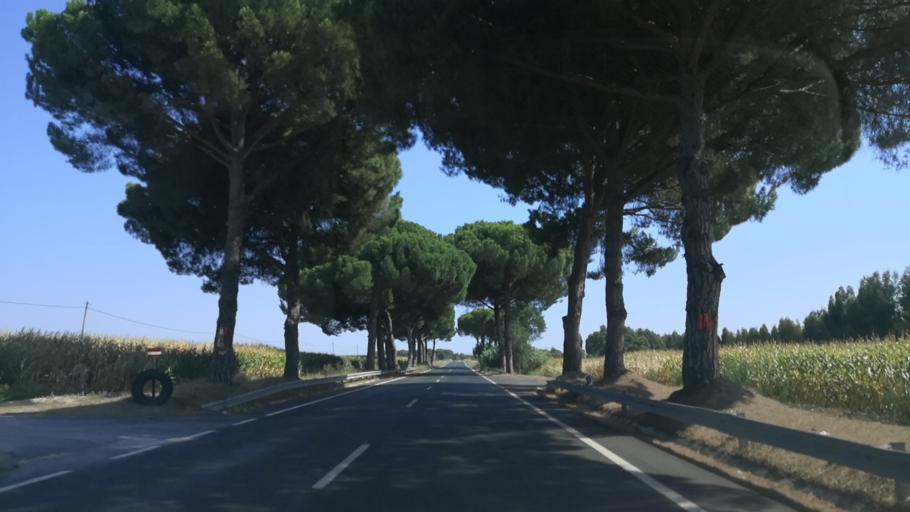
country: PT
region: Santarem
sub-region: Benavente
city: Poceirao
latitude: 38.7296
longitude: -8.6469
